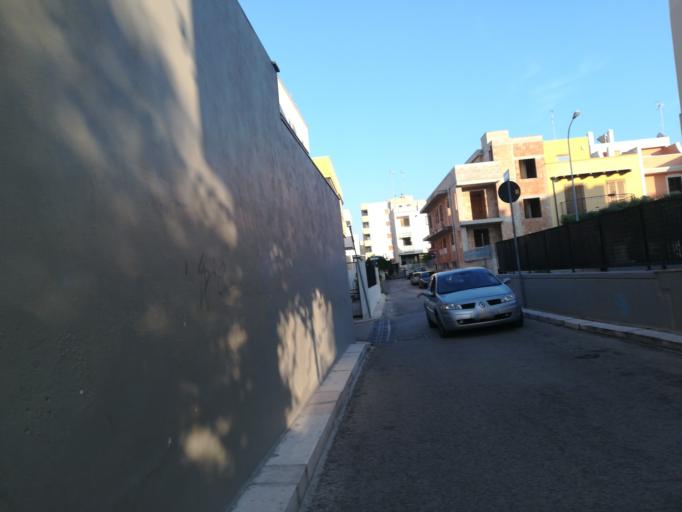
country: IT
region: Apulia
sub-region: Provincia di Bari
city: Polignano a Mare
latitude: 40.9932
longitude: 17.2267
